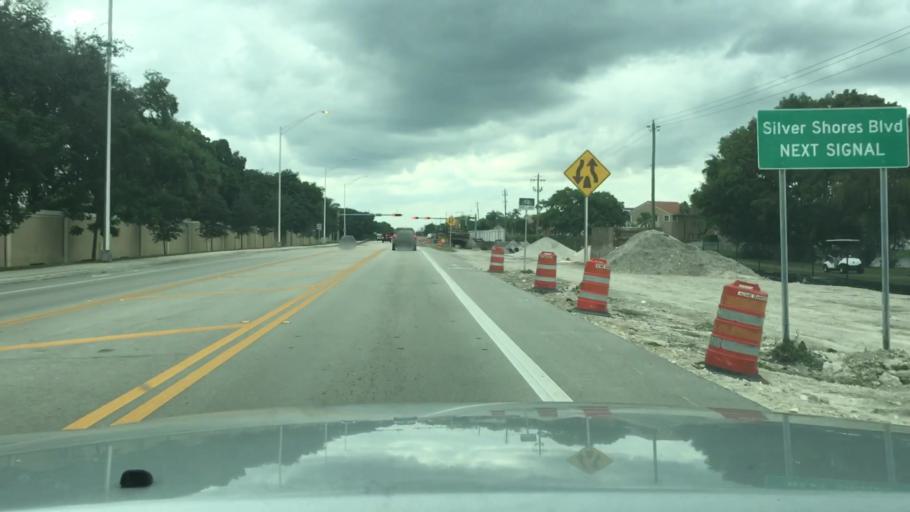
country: US
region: Florida
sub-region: Miami-Dade County
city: Country Club
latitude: 25.9932
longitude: -80.3499
